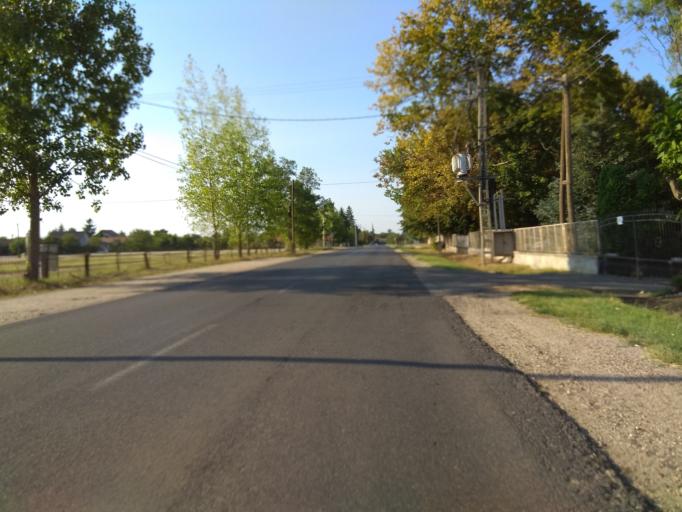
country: HU
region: Borsod-Abauj-Zemplen
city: Onod
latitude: 47.9954
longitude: 20.9211
